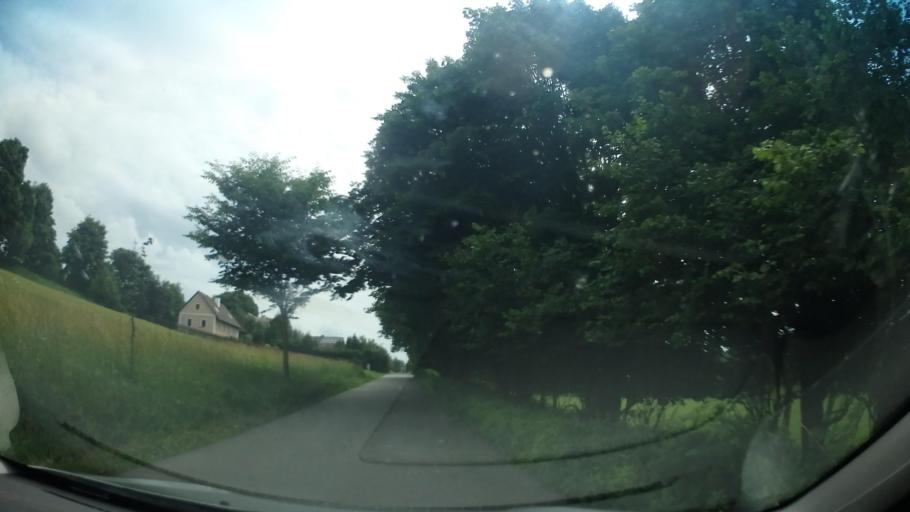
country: CZ
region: Vysocina
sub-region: Okres Zd'ar nad Sazavou
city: Nove Mesto na Morave
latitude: 49.5991
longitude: 16.0643
